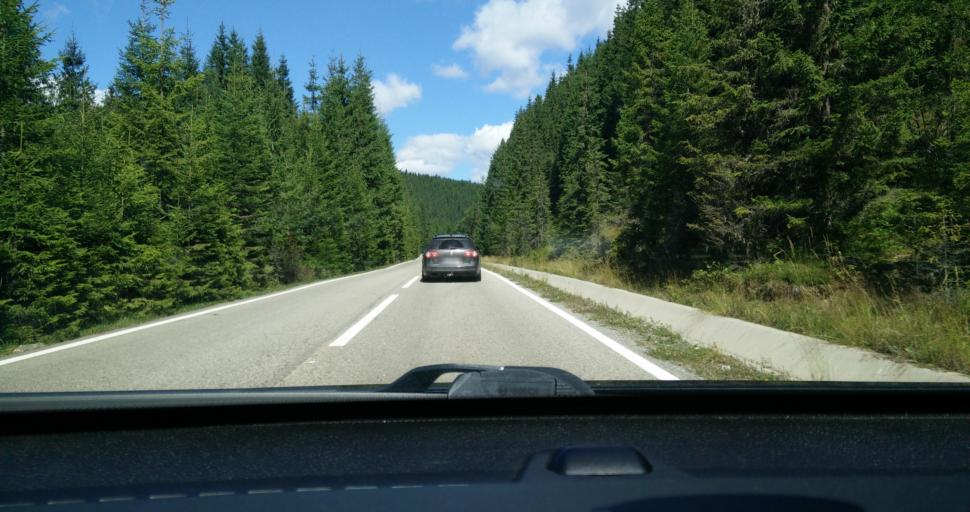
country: RO
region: Alba
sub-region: Comuna Sugag
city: Sugag
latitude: 45.5332
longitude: 23.6420
